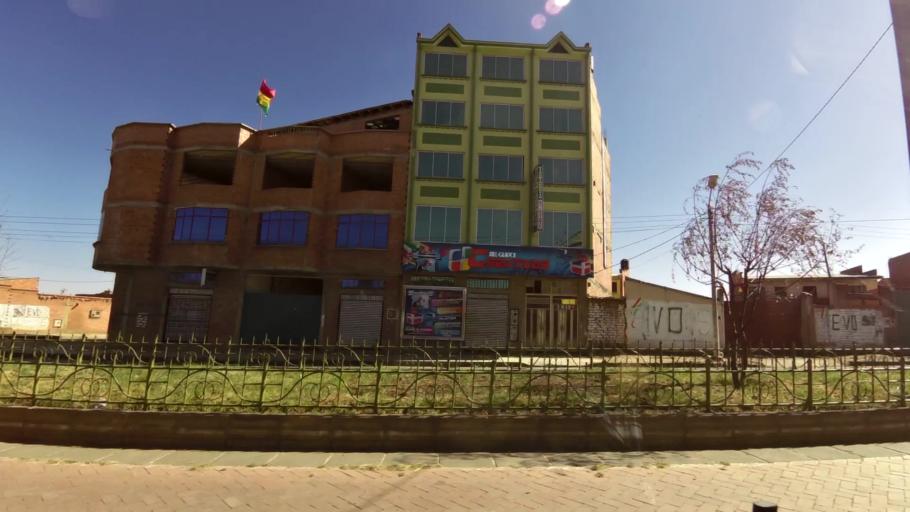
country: BO
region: La Paz
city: La Paz
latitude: -16.5169
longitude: -68.1816
